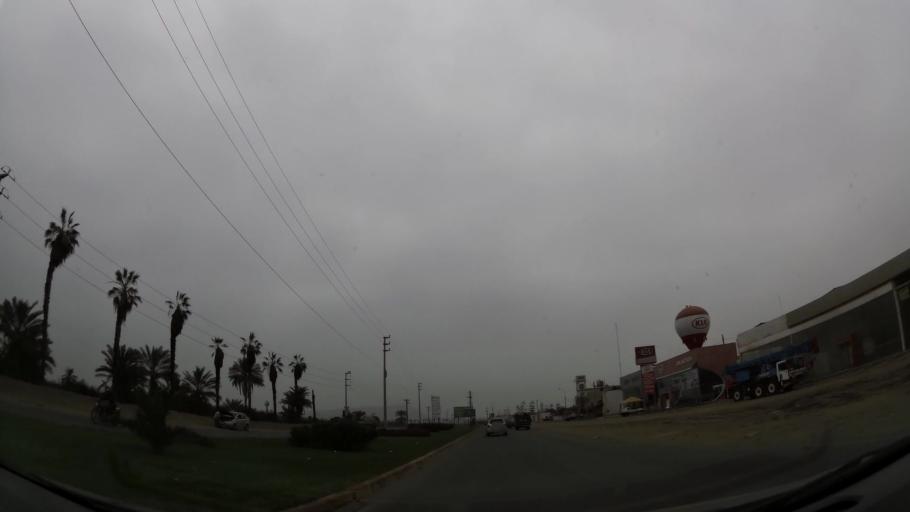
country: PE
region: Lima
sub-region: Lima
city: Surco
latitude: -12.2159
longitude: -76.9808
